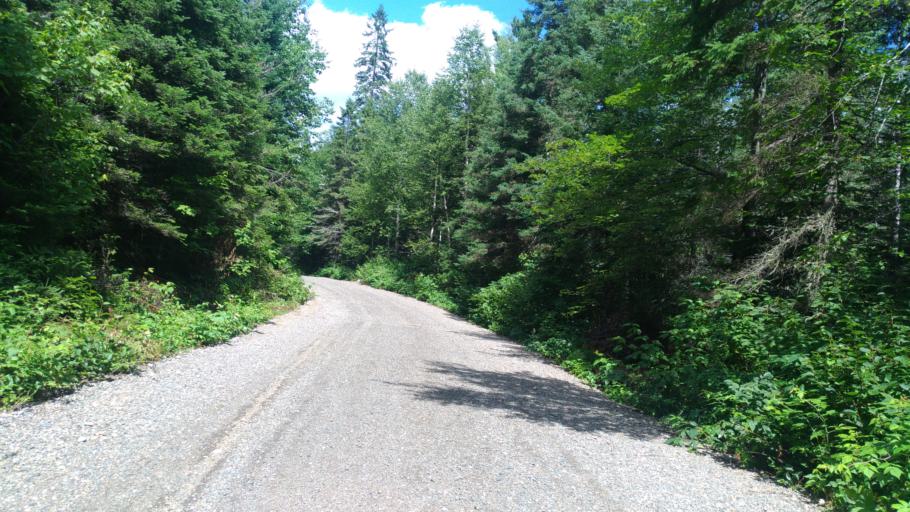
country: CA
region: Ontario
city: Rayside-Balfour
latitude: 46.5877
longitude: -81.5460
